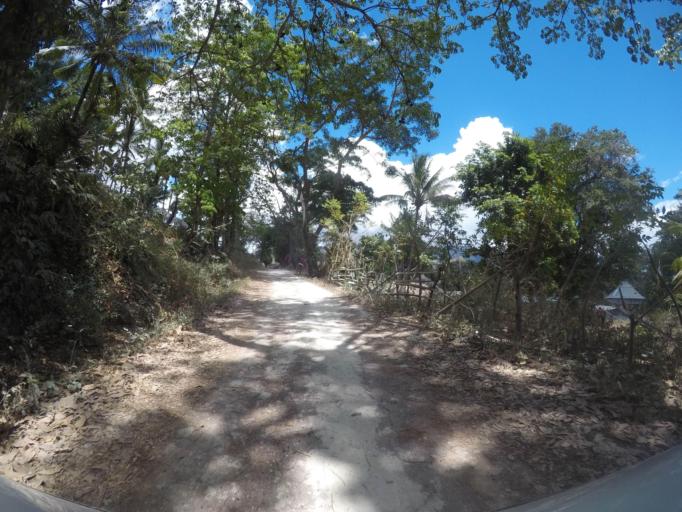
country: TL
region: Baucau
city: Baucau
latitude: -8.4866
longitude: 126.6417
